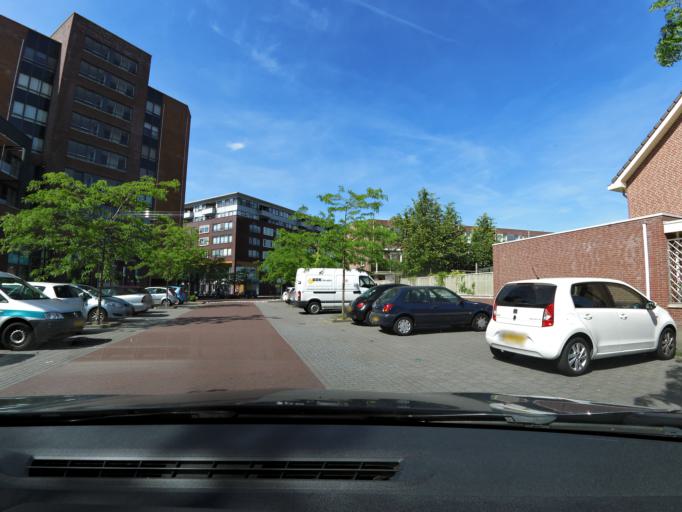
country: NL
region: South Holland
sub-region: Gemeente Binnenmaas
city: Heinenoord
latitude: 51.8457
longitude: 4.4983
